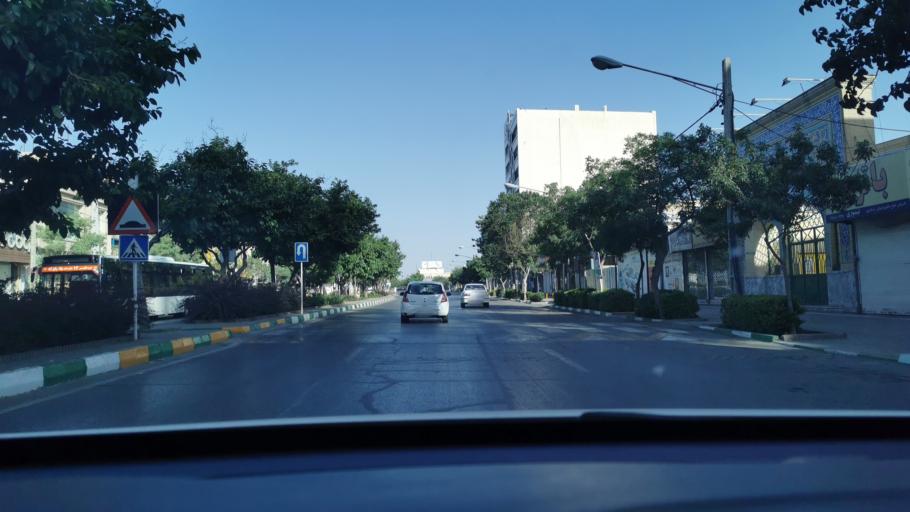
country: IR
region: Razavi Khorasan
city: Mashhad
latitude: 36.3326
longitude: 59.5153
